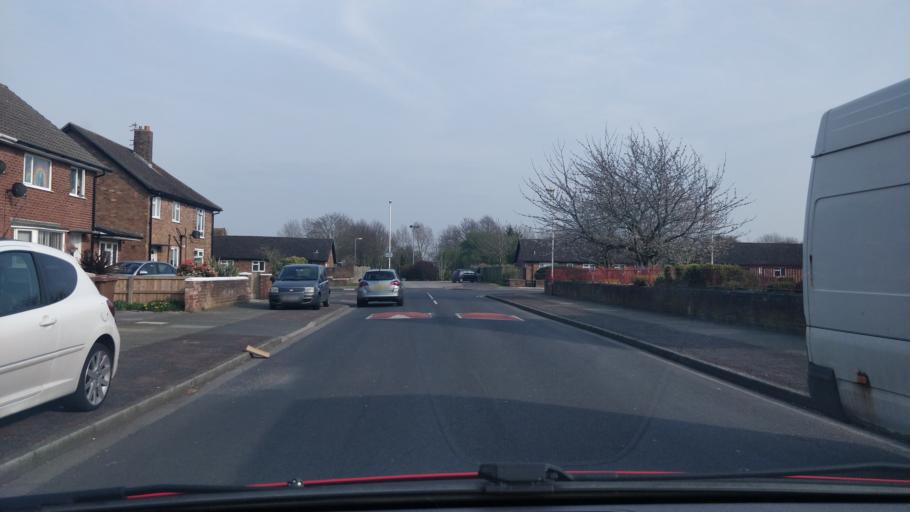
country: GB
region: England
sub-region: Sefton
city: Formby
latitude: 53.5961
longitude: -3.0352
